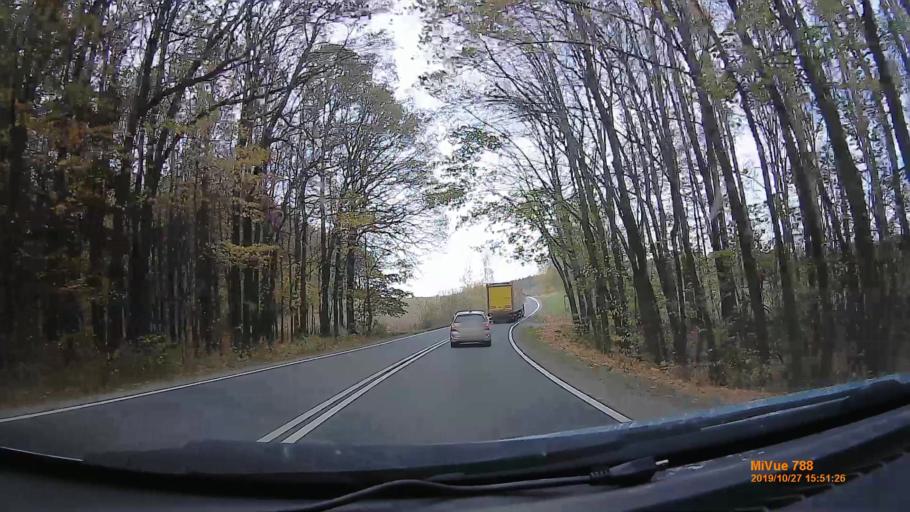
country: PL
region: Lower Silesian Voivodeship
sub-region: Powiat klodzki
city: Bozkow
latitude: 50.5261
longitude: 16.5818
